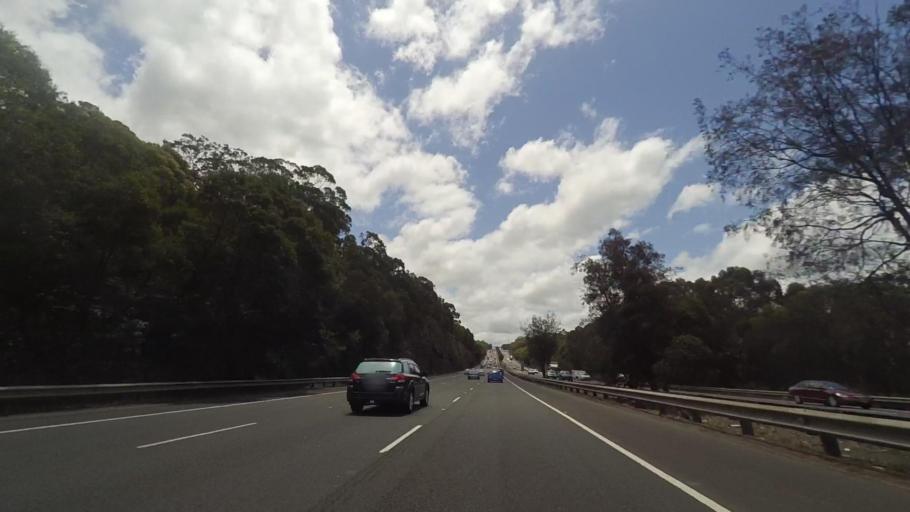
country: AU
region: New South Wales
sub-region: Hornsby Shire
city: Mount Colah
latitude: -33.6920
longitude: 151.1214
